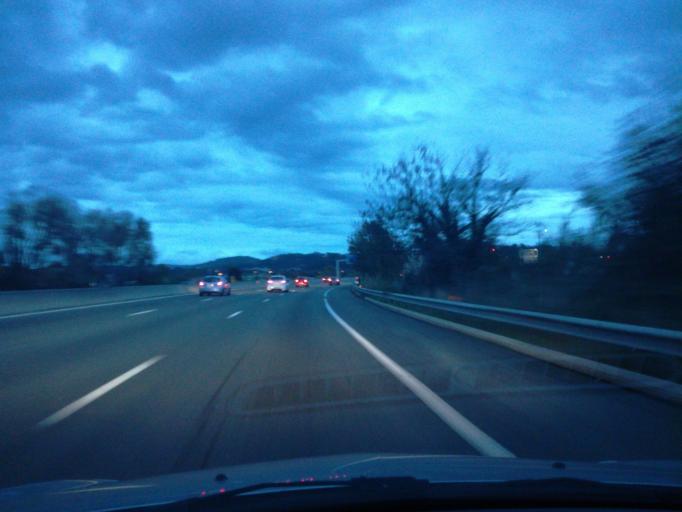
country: FR
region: Provence-Alpes-Cote d'Azur
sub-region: Departement des Alpes-Maritimes
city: Mandelieu-la-Napoule
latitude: 43.5558
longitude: 6.9462
